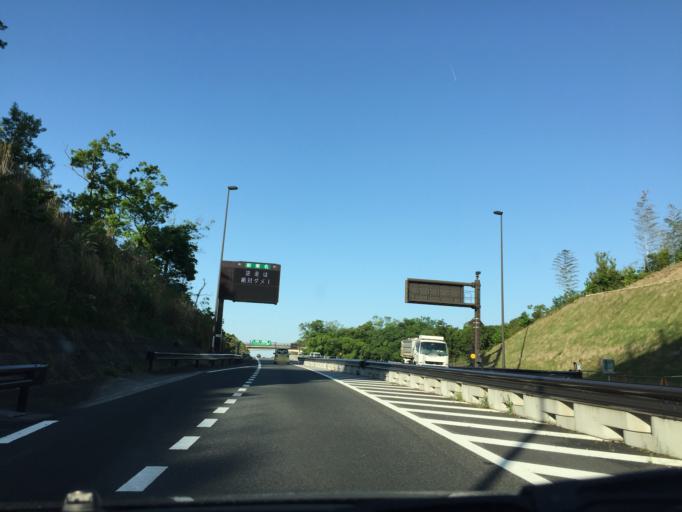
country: JP
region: Shizuoka
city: Mishima
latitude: 35.1537
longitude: 138.8839
